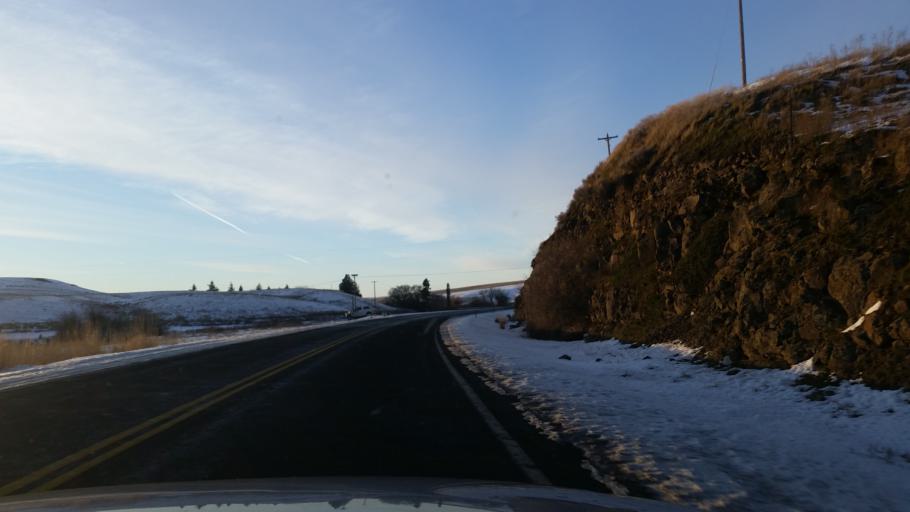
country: US
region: Washington
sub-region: Whitman County
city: Colfax
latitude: 47.1149
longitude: -117.6614
